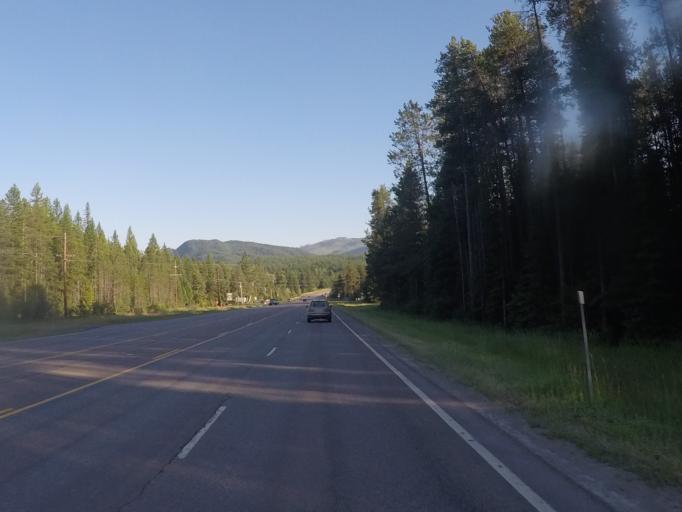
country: US
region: Montana
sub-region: Flathead County
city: Columbia Falls
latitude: 48.4009
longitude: -114.0427
